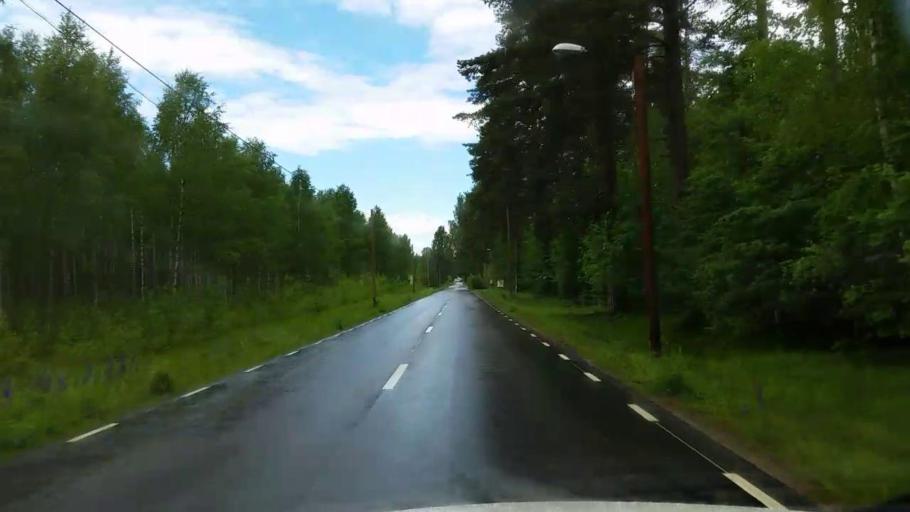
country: SE
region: Gaevleborg
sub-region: Sandvikens Kommun
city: Jarbo
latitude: 60.8391
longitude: 16.4828
